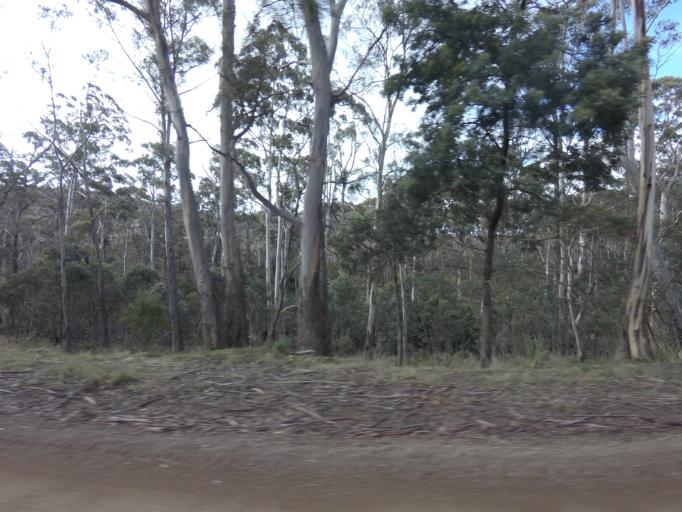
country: AU
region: Tasmania
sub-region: Derwent Valley
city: New Norfolk
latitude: -42.7511
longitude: 146.8760
